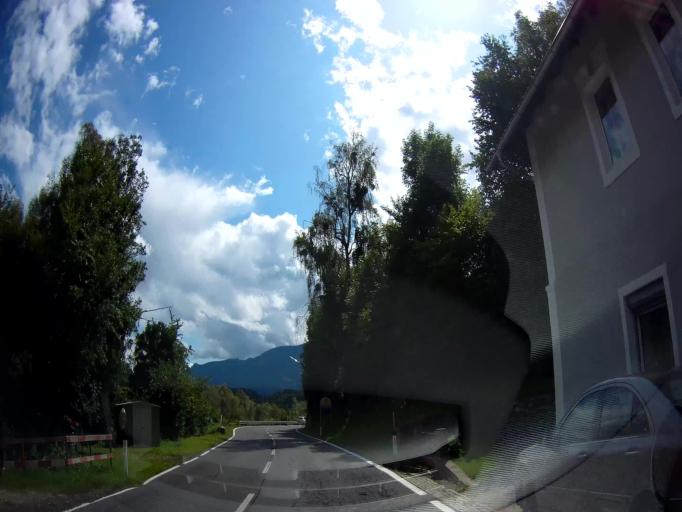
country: AT
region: Carinthia
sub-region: Politischer Bezirk Spittal an der Drau
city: Seeboden
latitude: 46.8310
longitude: 13.4925
